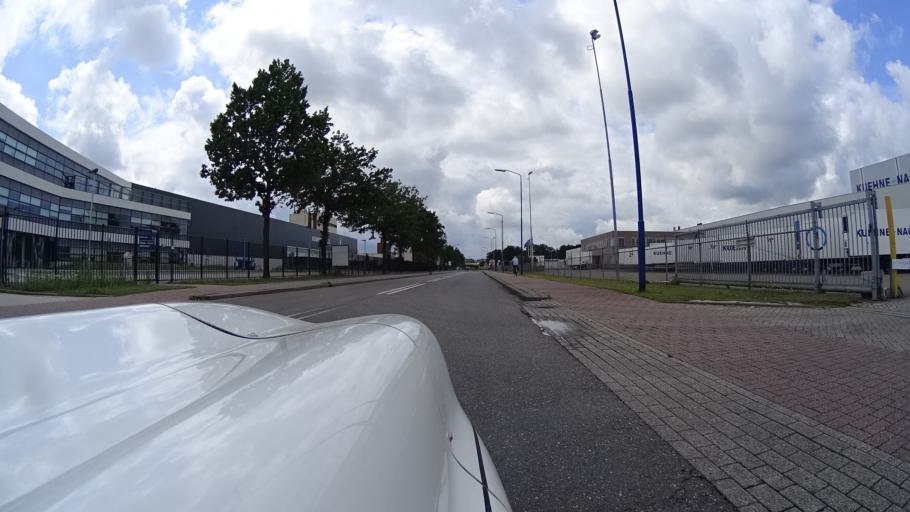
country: NL
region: North Brabant
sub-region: Gemeente Veghel
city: Eerde
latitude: 51.6096
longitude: 5.5158
